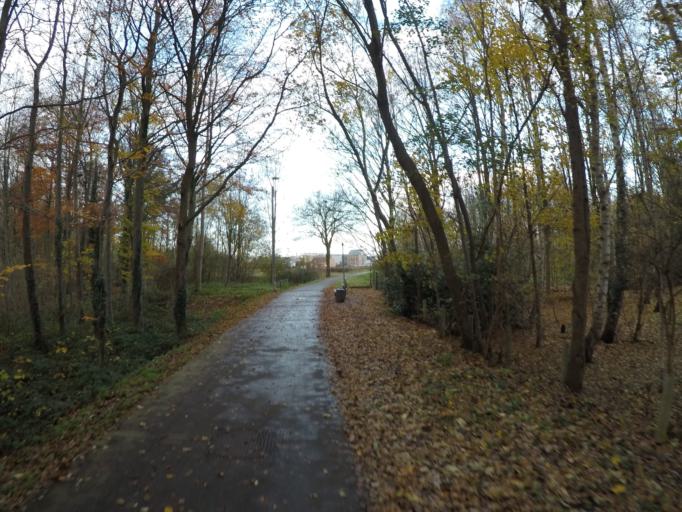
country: BE
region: Flanders
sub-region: Provincie Vlaams-Brabant
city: Londerzeel
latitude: 51.0064
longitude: 4.2942
